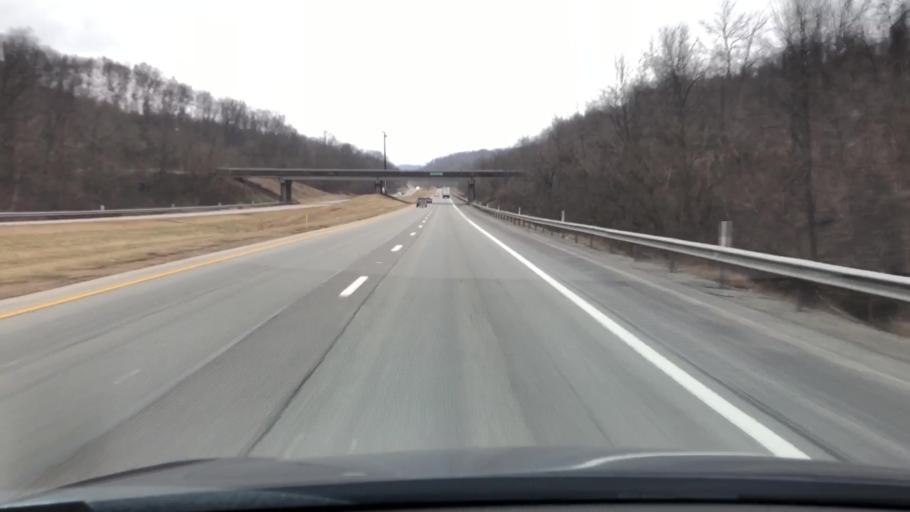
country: US
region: Pennsylvania
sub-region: Washington County
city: East Washington
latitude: 40.0554
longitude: -80.1856
